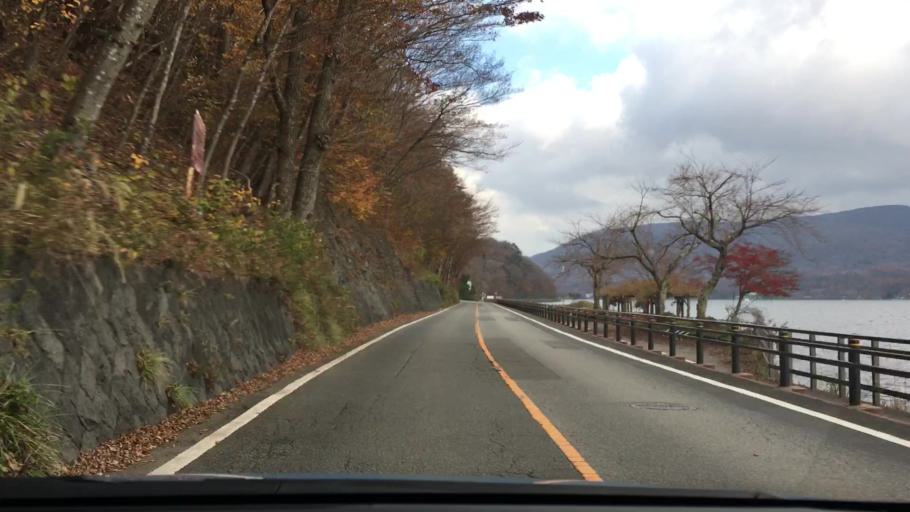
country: JP
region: Shizuoka
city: Gotemba
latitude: 35.4261
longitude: 138.8755
